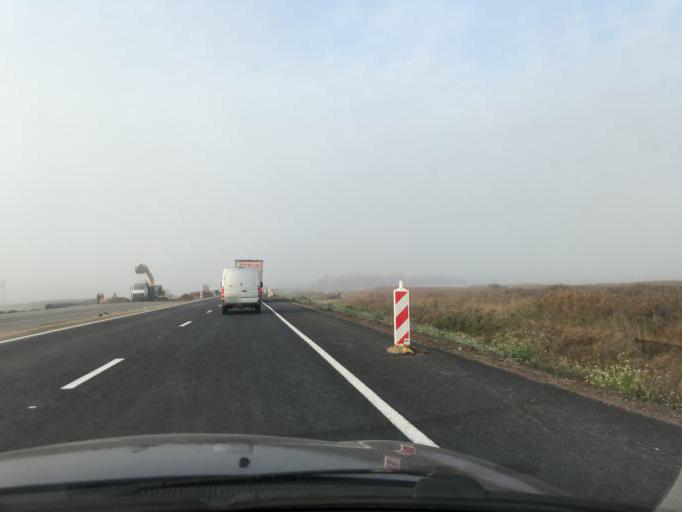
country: BY
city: Berezovka
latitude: 53.8353
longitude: 25.4652
